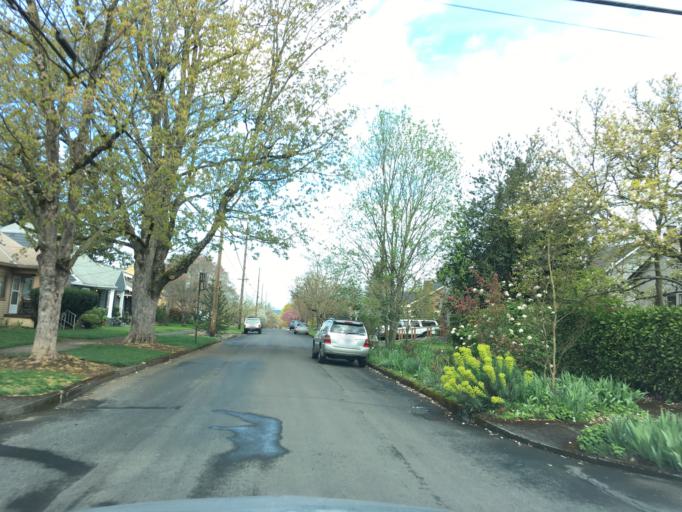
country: US
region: Oregon
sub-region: Multnomah County
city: Lents
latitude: 45.5495
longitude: -122.5973
